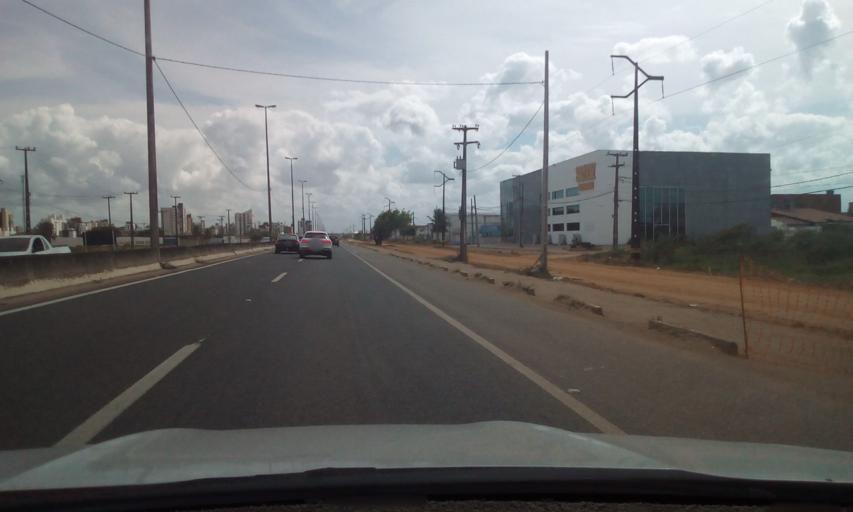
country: BR
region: Paraiba
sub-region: Cabedelo
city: Cabedelo
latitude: -7.0290
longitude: -34.8399
